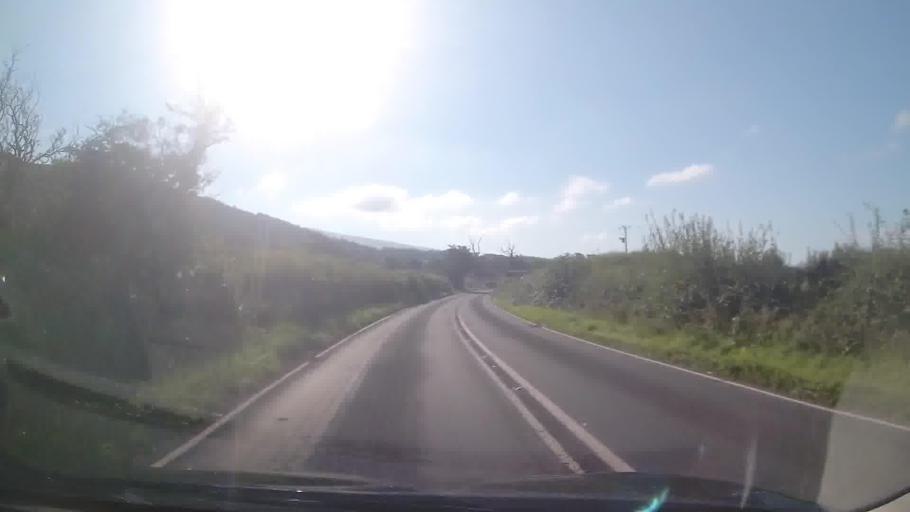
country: GB
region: England
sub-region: Cumbria
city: Seascale
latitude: 54.3503
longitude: -3.3652
